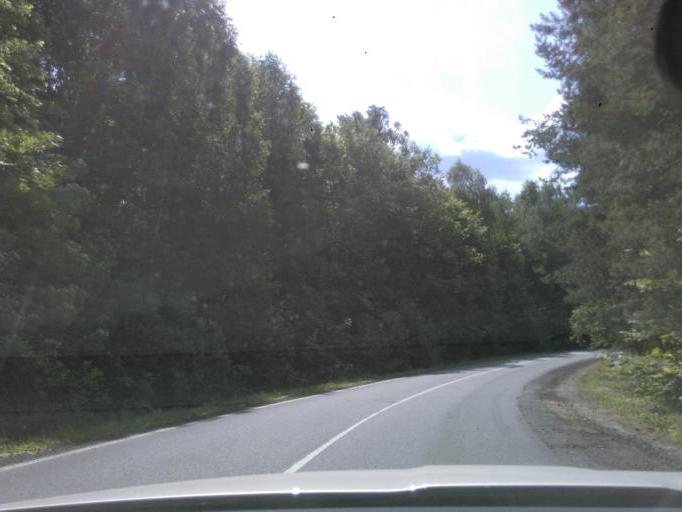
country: RU
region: Moskovskaya
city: Solnechnogorsk
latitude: 56.1560
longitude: 36.9824
